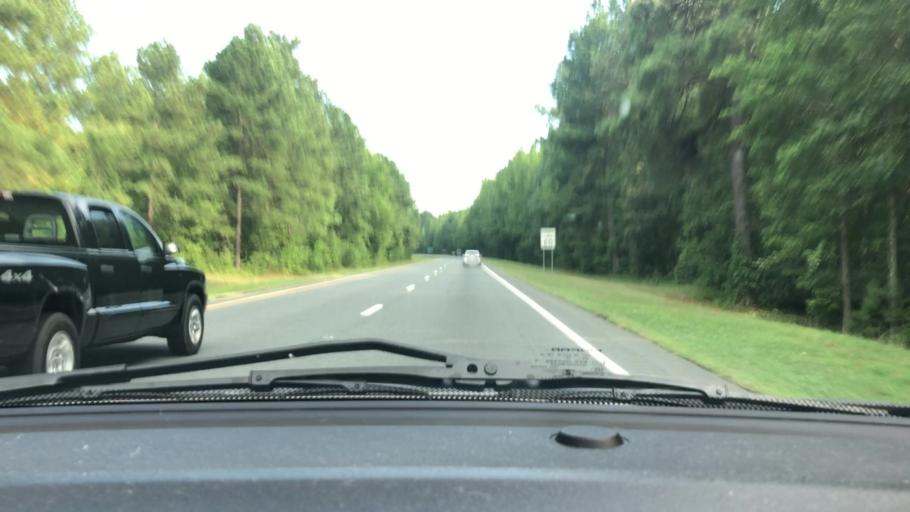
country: US
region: North Carolina
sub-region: Guilford County
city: Forest Oaks
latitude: 35.9090
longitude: -79.6729
